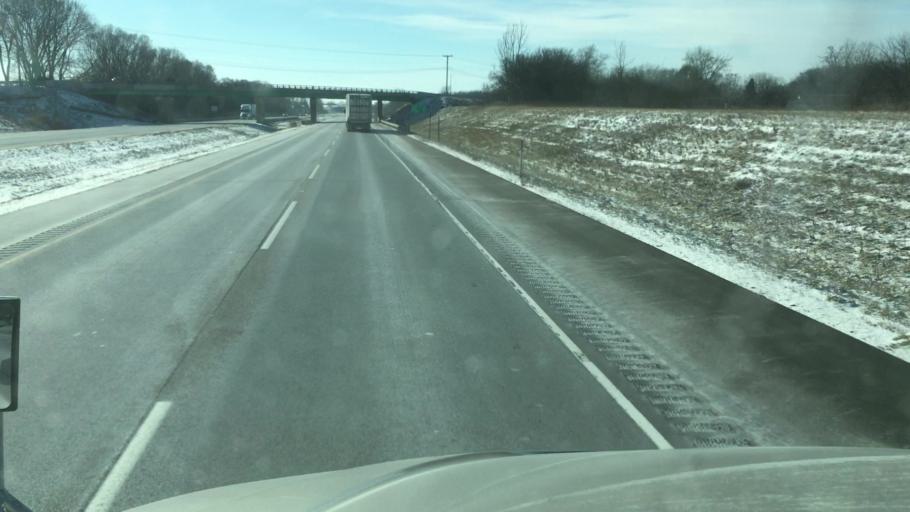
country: US
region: Indiana
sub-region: Saint Joseph County
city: Granger
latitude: 41.7255
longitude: -86.1530
